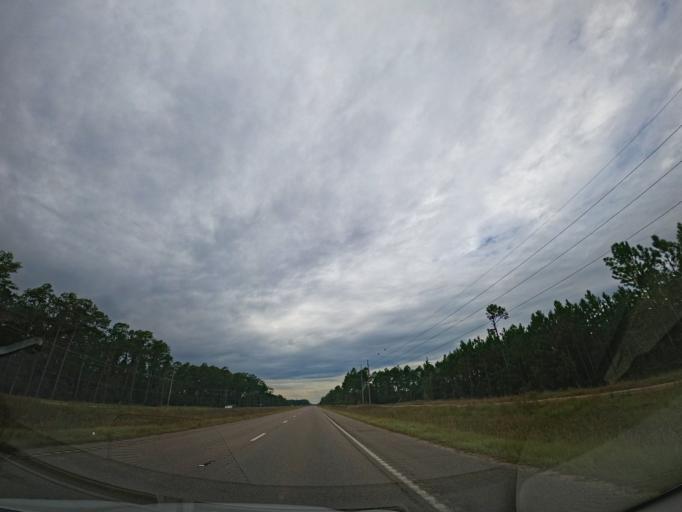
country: US
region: Mississippi
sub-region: Hancock County
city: Waveland
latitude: 30.3012
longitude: -89.4821
